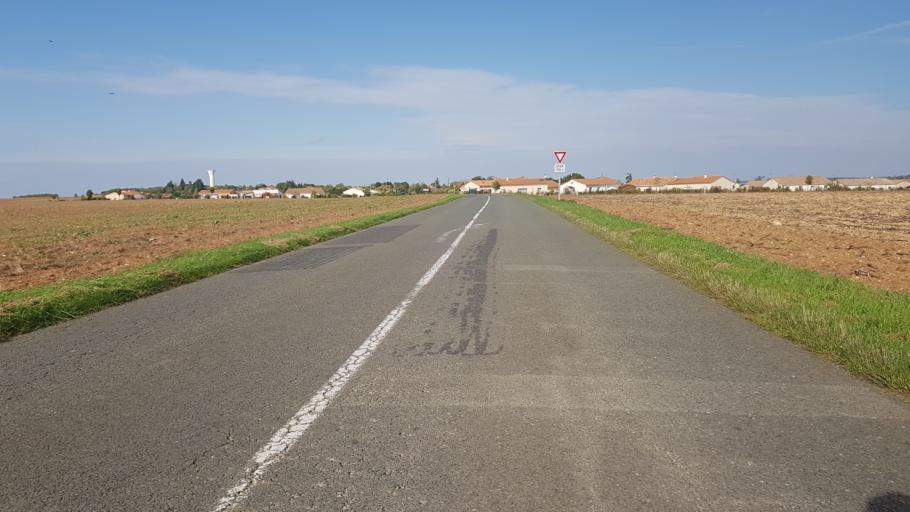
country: FR
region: Poitou-Charentes
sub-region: Departement de la Vienne
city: Chasseneuil-du-Poitou
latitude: 46.6544
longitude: 0.3406
